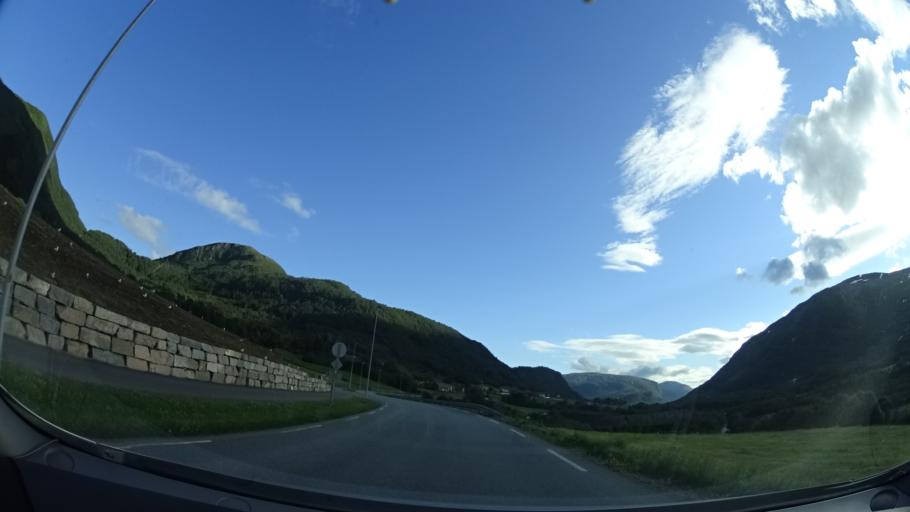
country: NO
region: More og Romsdal
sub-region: Gjemnes
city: Batnfjordsora
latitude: 62.8799
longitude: 7.6519
